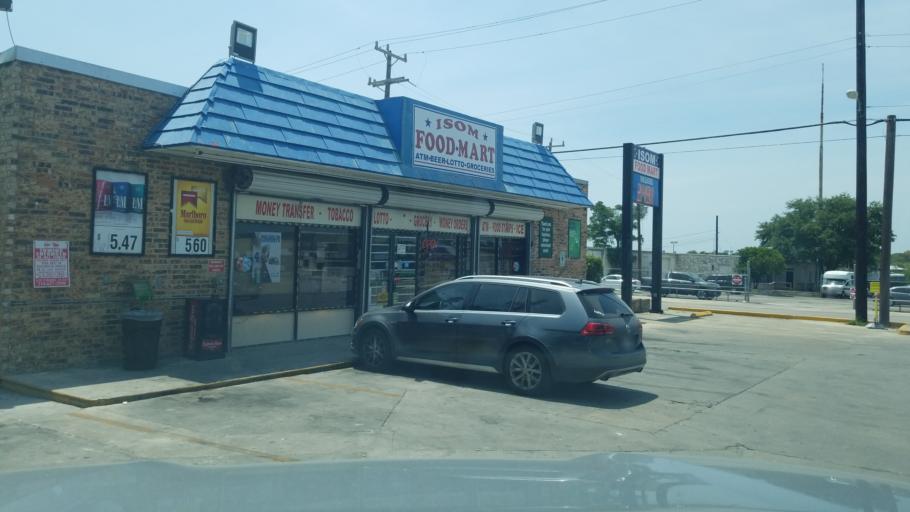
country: US
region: Texas
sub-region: Bexar County
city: Castle Hills
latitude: 29.5281
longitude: -98.4929
